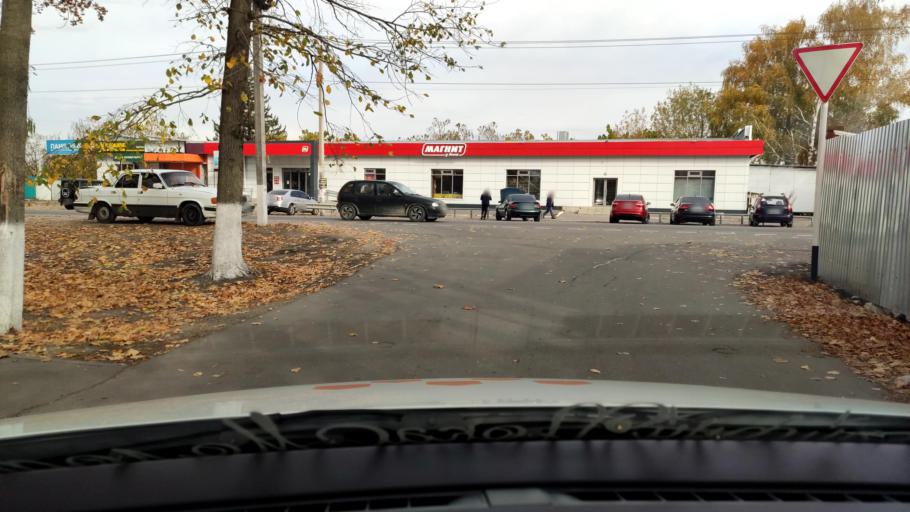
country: RU
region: Voronezj
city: Ramon'
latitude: 51.9102
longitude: 39.3309
